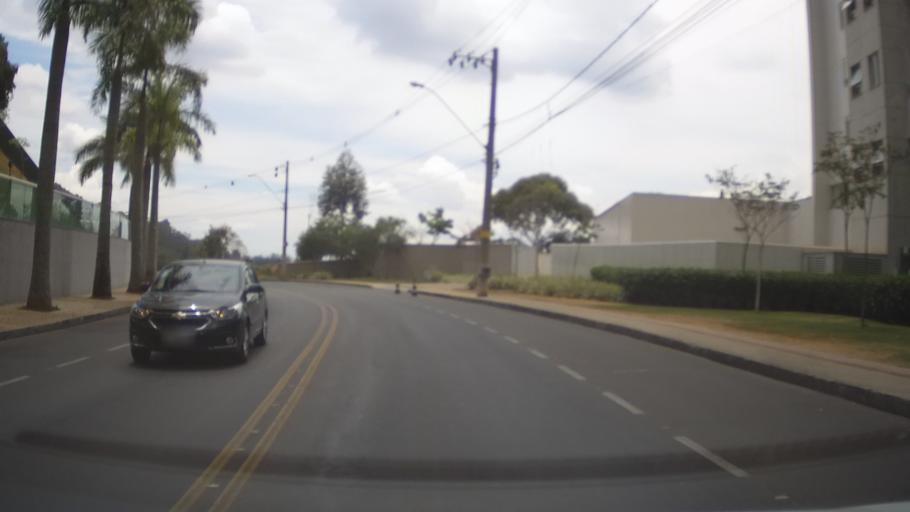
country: BR
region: Minas Gerais
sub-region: Belo Horizonte
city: Belo Horizonte
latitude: -19.9719
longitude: -43.9254
